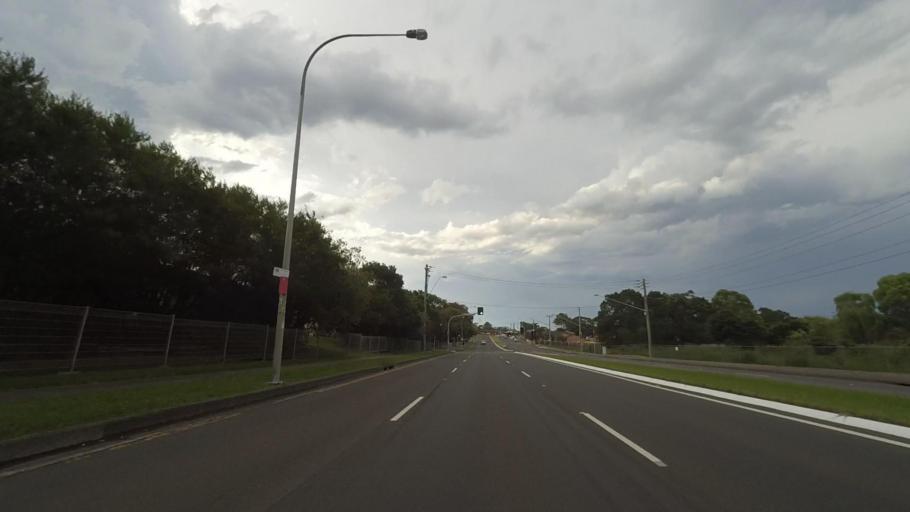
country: AU
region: New South Wales
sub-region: Shellharbour
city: Barrack Heights
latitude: -34.5702
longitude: 150.8618
